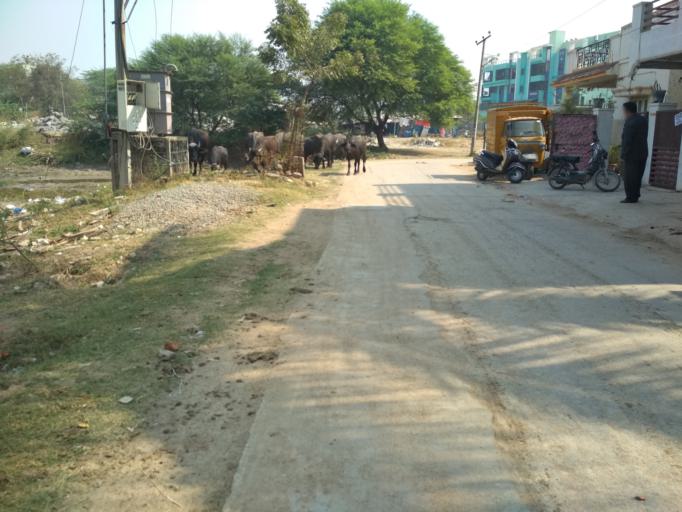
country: IN
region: Telangana
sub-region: Rangareddi
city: Uppal Kalan
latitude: 17.4204
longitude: 78.5764
